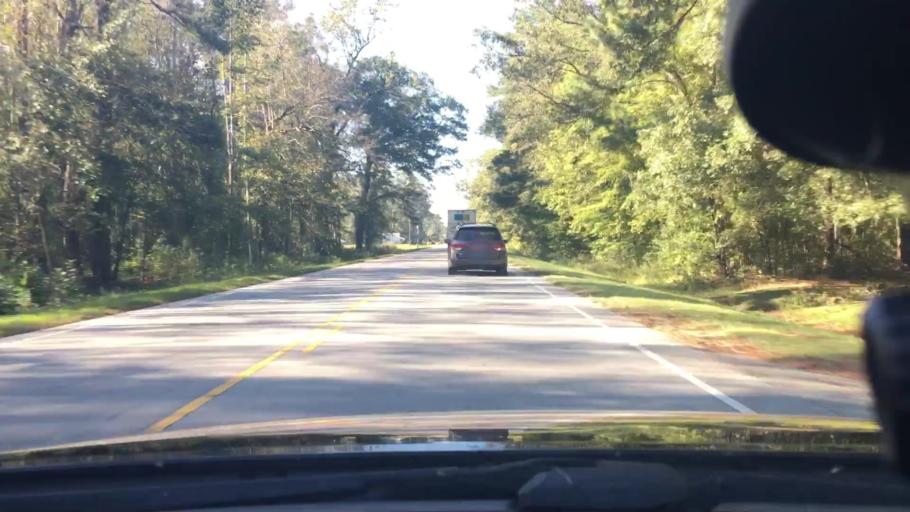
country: US
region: North Carolina
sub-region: Craven County
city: Vanceboro
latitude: 35.2629
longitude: -77.1033
